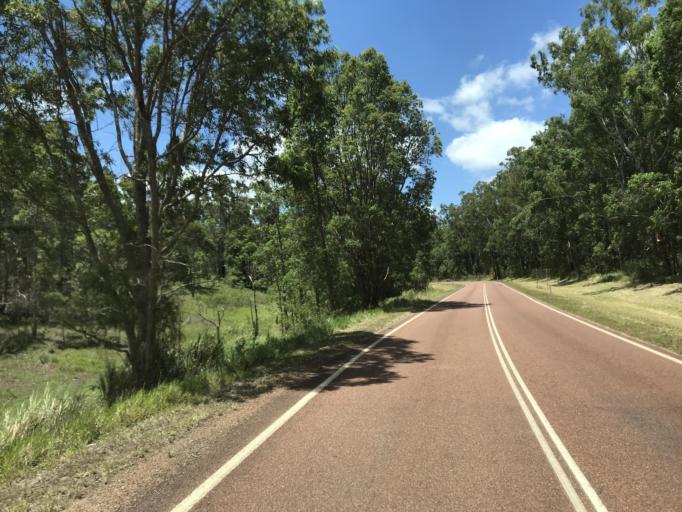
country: AU
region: Queensland
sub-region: Tablelands
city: Ravenshoe
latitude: -17.5944
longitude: 145.4767
